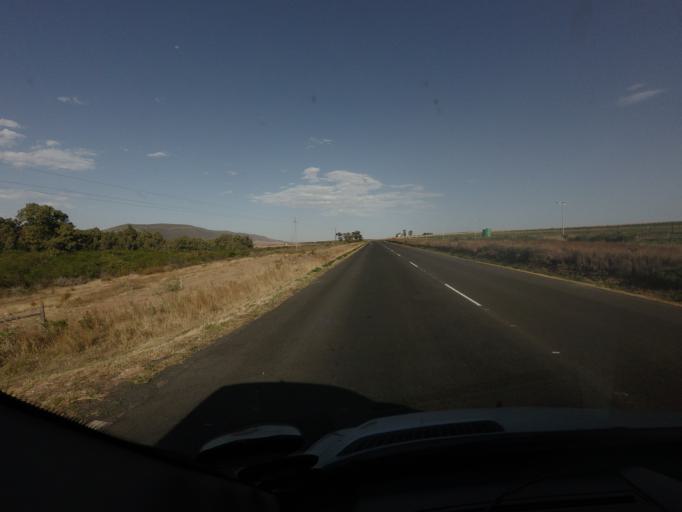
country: ZA
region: Western Cape
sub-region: Cape Winelands District Municipality
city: Ashton
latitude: -34.0910
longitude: 20.1152
